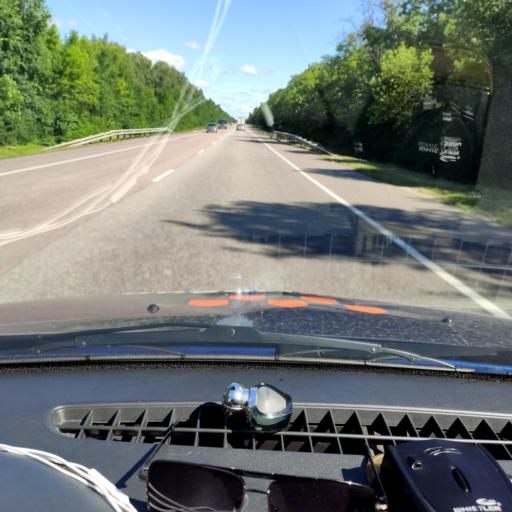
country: RU
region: Lipetsk
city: Khlevnoye
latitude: 52.2854
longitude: 39.1678
